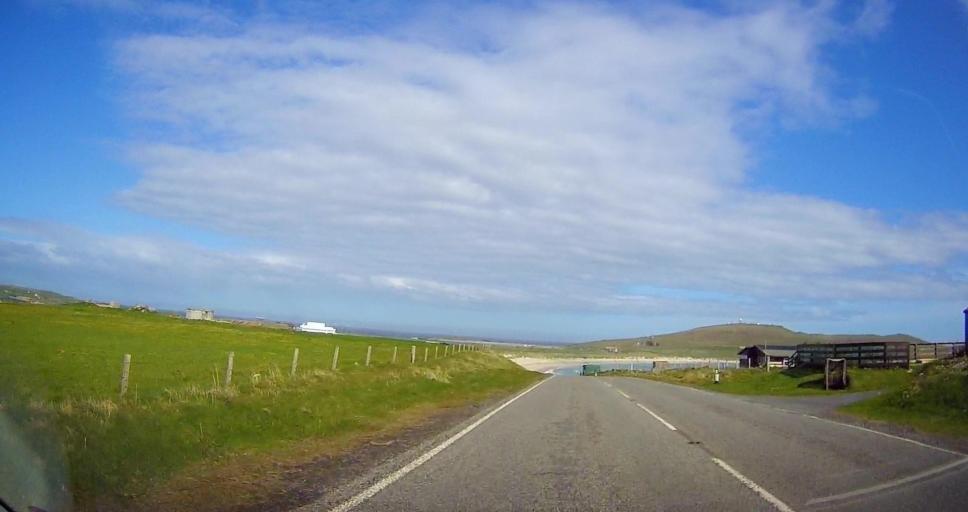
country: GB
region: Scotland
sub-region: Shetland Islands
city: Sandwick
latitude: 59.8762
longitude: -1.3049
